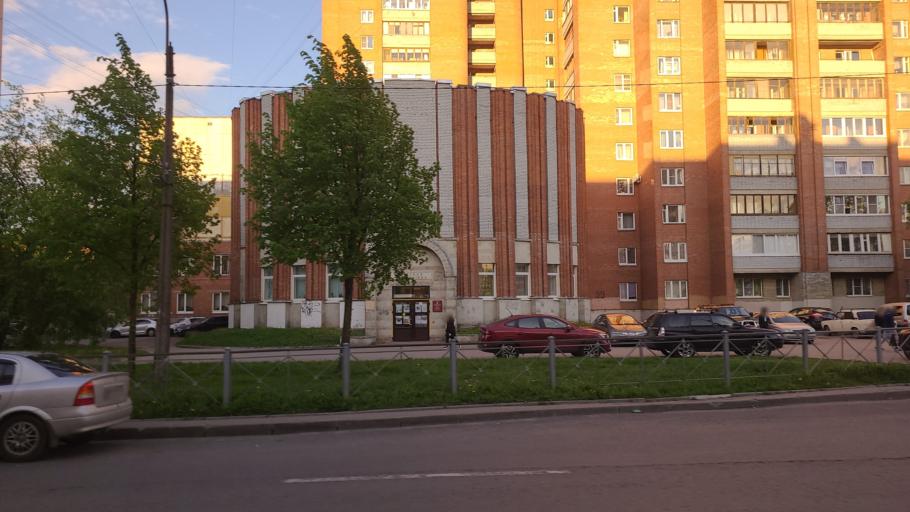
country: RU
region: St.-Petersburg
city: Kolpino
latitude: 59.7362
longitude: 30.5794
